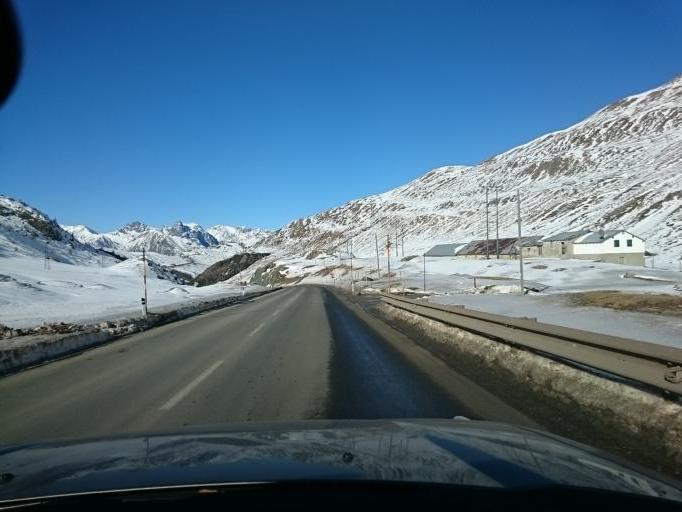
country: IT
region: Lombardy
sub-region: Provincia di Sondrio
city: Livigno
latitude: 46.5072
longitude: 10.1995
